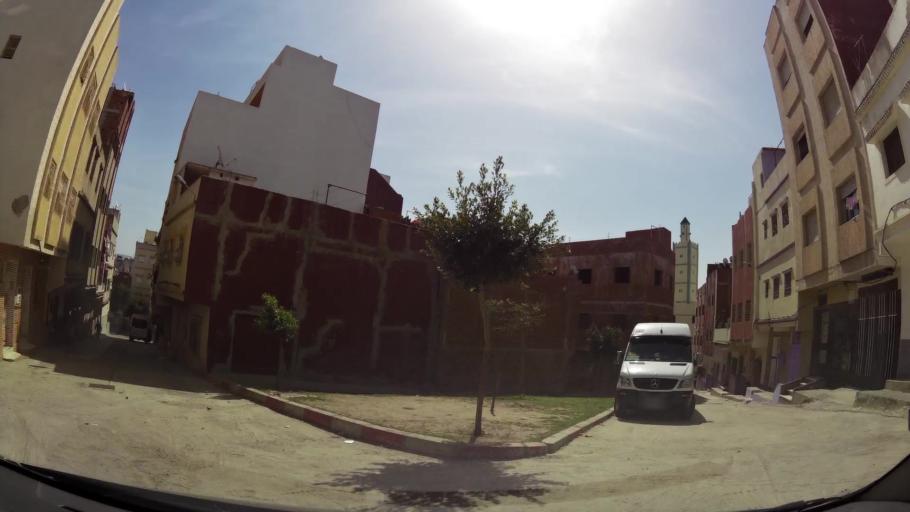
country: MA
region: Tanger-Tetouan
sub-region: Tanger-Assilah
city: Tangier
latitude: 35.7412
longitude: -5.8028
